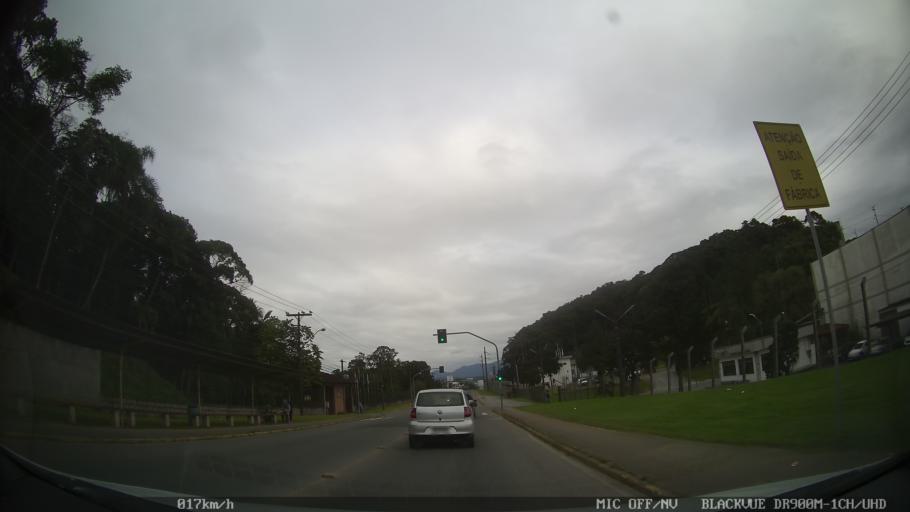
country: BR
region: Santa Catarina
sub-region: Joinville
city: Joinville
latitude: -26.2608
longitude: -48.8557
